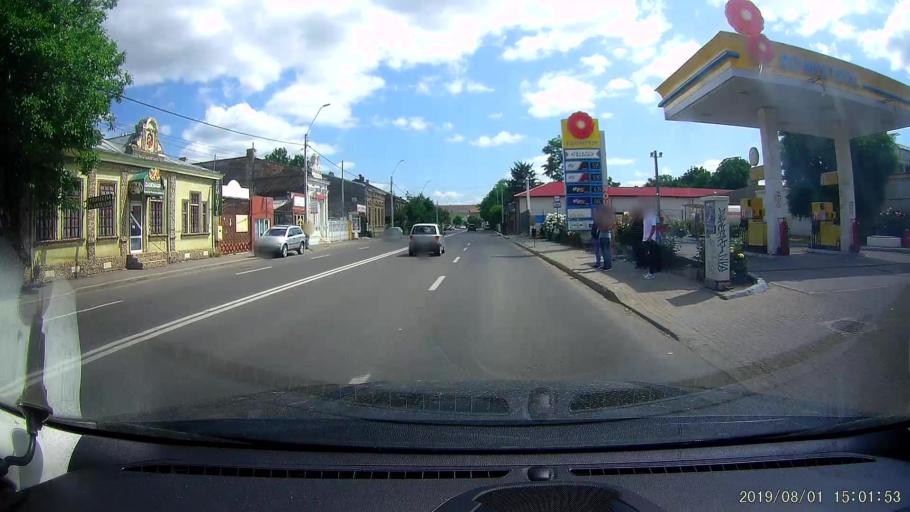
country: RO
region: Braila
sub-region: Municipiul Braila
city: Braila
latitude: 45.2707
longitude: 27.9603
